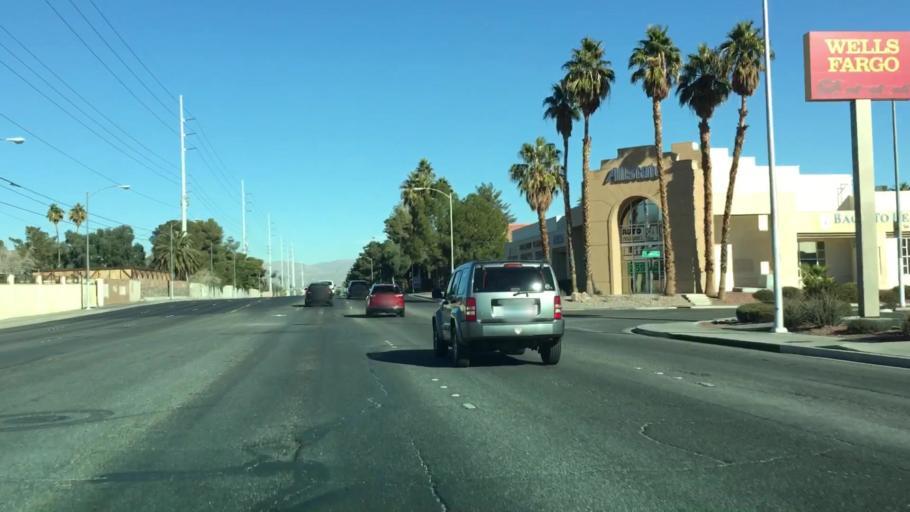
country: US
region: Nevada
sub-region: Clark County
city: Winchester
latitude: 36.1034
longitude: -115.1190
